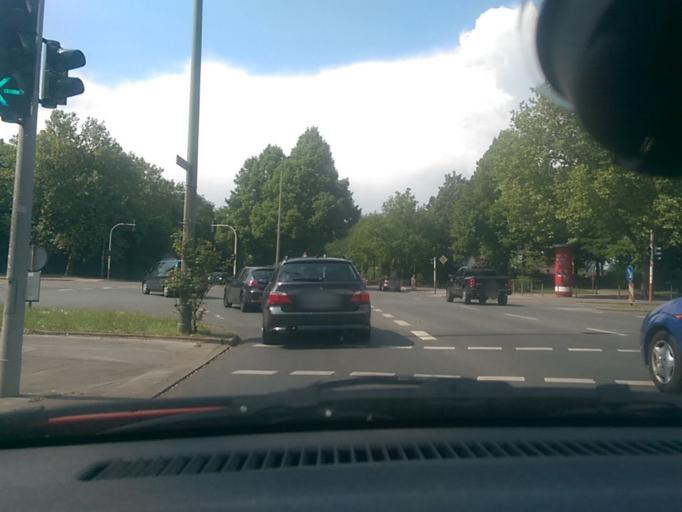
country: DE
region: North Rhine-Westphalia
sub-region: Regierungsbezirk Munster
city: Gladbeck
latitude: 51.5301
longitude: 7.0350
